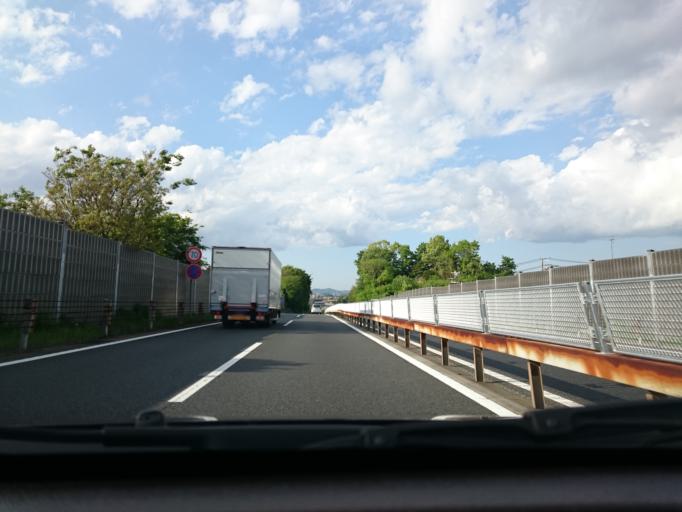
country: JP
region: Kanagawa
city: Oiso
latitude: 35.3435
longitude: 139.2967
